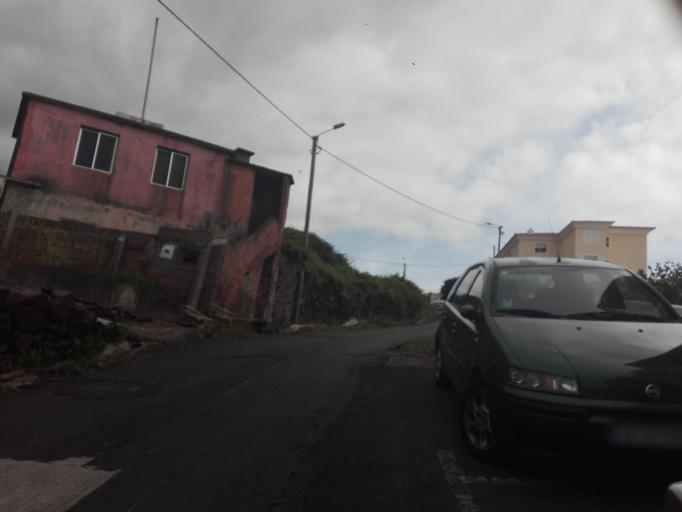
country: PT
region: Madeira
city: Canico
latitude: 32.6513
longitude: -16.8269
